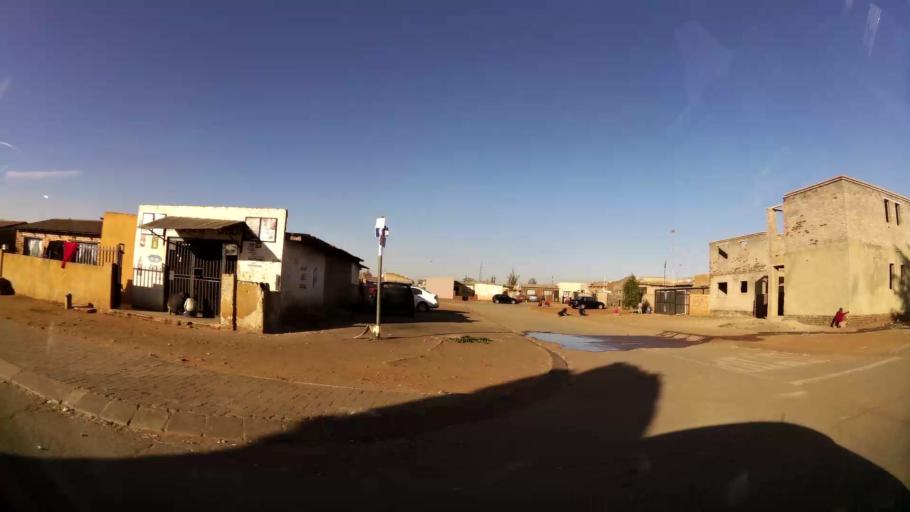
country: ZA
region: Gauteng
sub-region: Ekurhuleni Metropolitan Municipality
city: Tembisa
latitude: -26.0064
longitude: 28.2393
